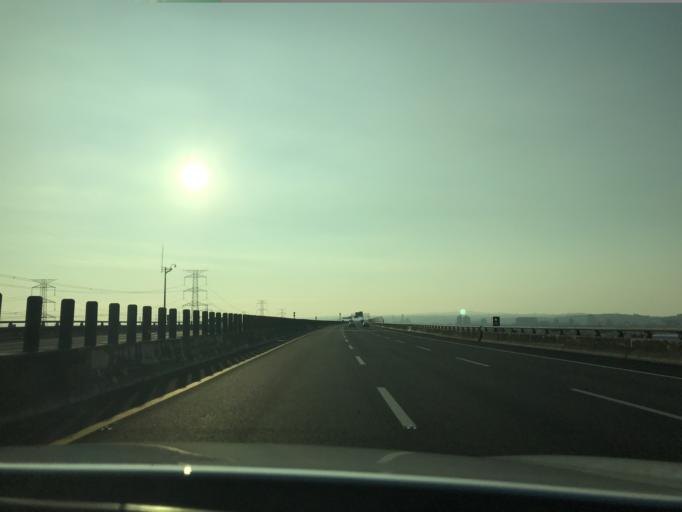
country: TW
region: Taiwan
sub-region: Changhua
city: Chang-hua
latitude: 24.1184
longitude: 120.5373
